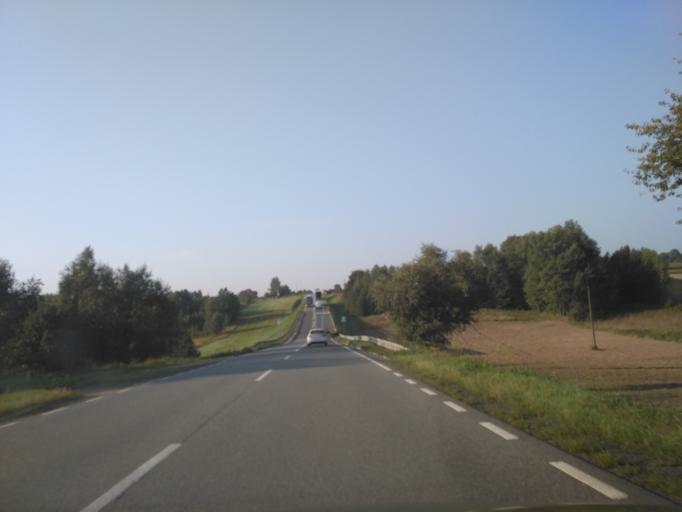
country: PL
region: Lublin Voivodeship
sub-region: Powiat janowski
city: Modliborzyce
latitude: 50.8001
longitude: 22.3190
